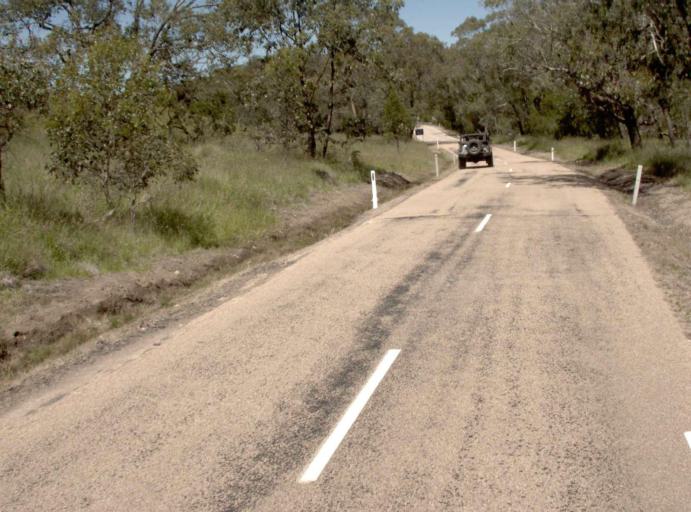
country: AU
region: Victoria
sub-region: East Gippsland
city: Lakes Entrance
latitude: -37.2303
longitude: 148.2624
